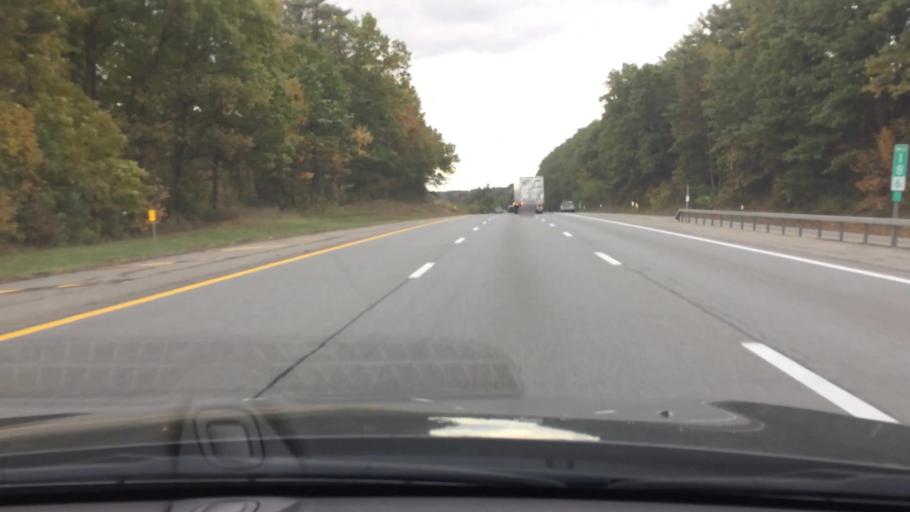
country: US
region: New York
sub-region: Saratoga County
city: Country Knolls
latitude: 42.9362
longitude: -73.8045
